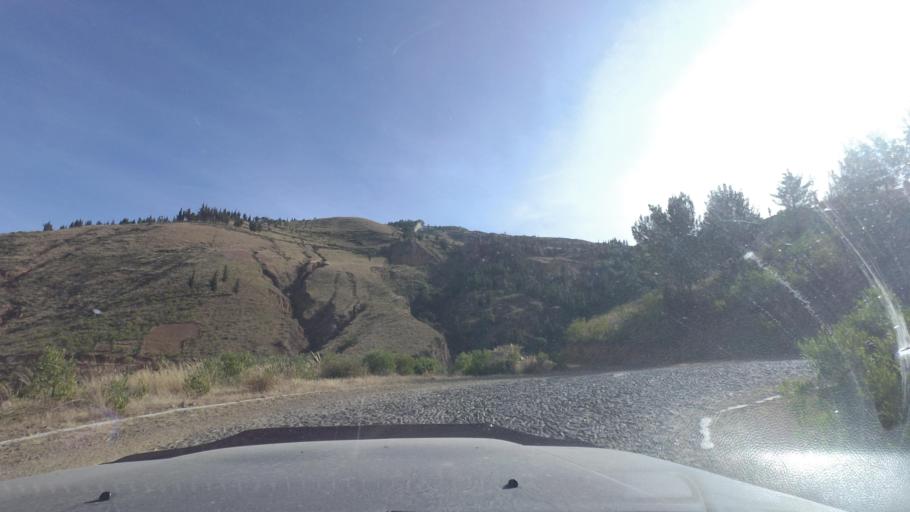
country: BO
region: Cochabamba
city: Cochabamba
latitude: -17.3744
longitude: -66.0268
